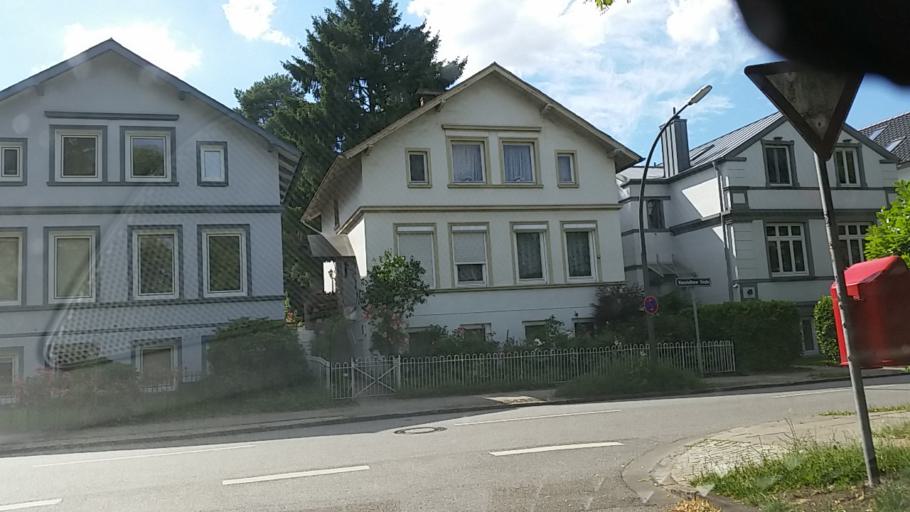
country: DE
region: Schleswig-Holstein
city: Halstenbek
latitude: 53.5559
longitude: 9.8449
